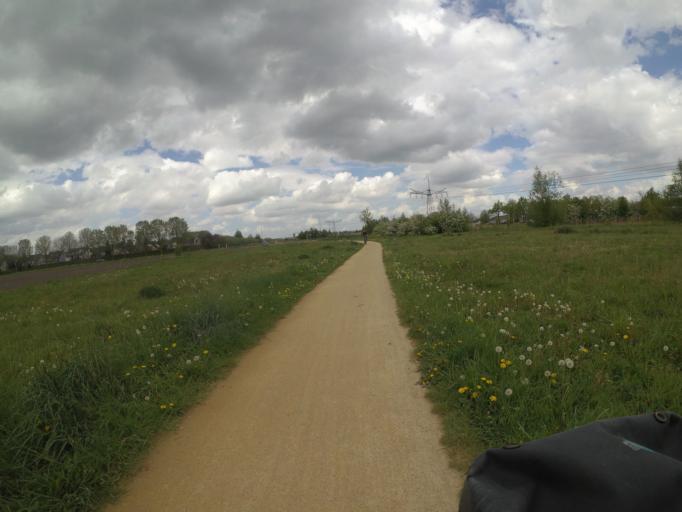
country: NL
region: North Brabant
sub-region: Gemeente Dongen
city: Dongen
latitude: 51.6335
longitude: 4.9561
